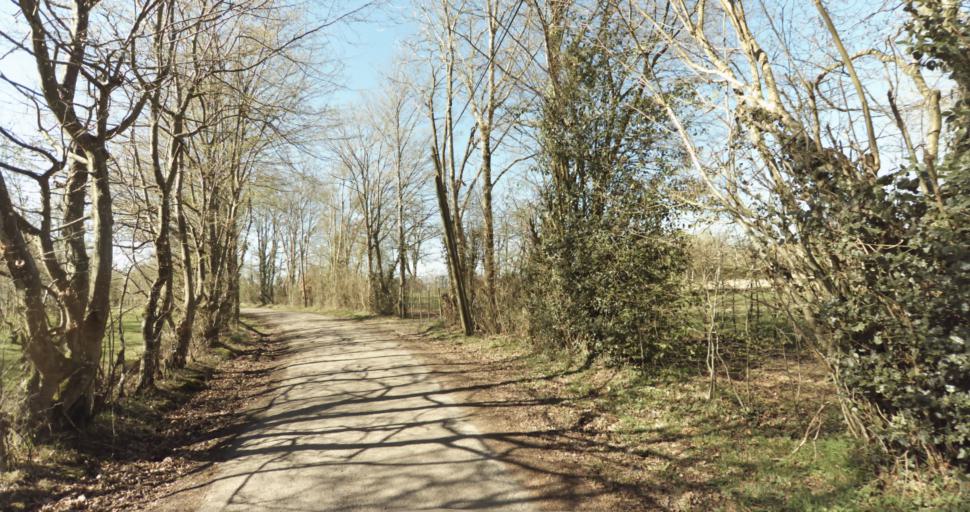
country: FR
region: Lower Normandy
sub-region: Departement du Calvados
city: Livarot
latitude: 48.9589
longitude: 0.0829
